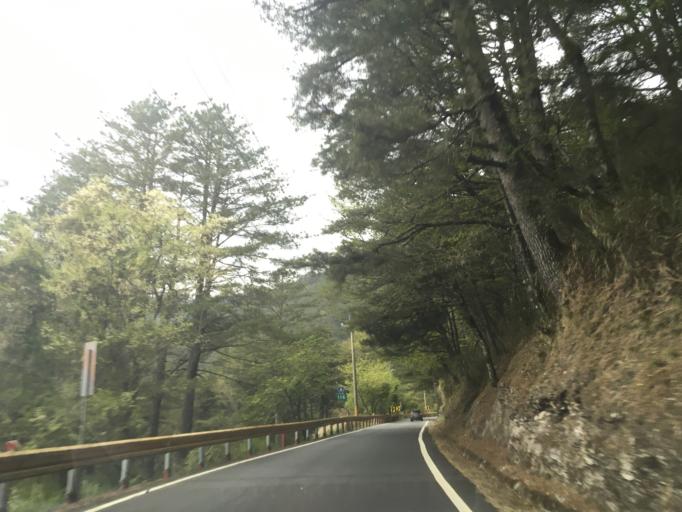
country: TW
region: Taiwan
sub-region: Hualien
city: Hualian
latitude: 24.1865
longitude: 121.3363
